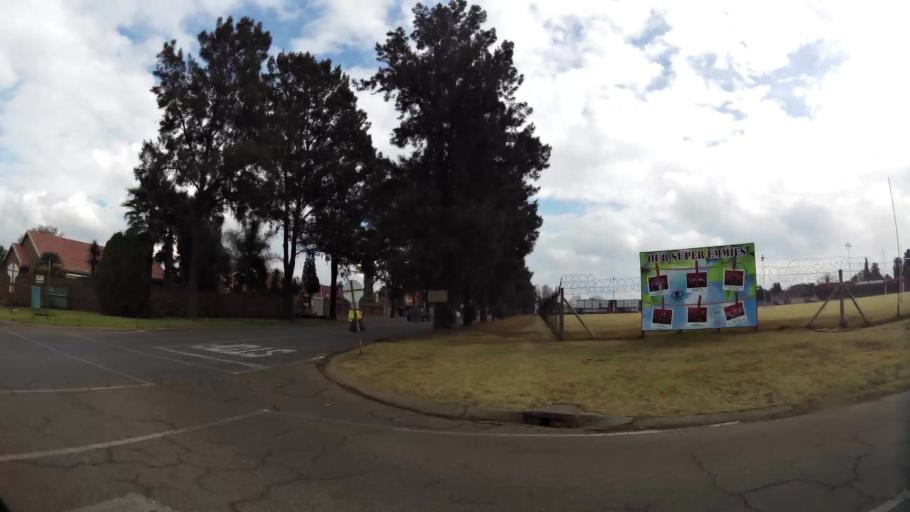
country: ZA
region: Gauteng
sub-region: Sedibeng District Municipality
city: Vanderbijlpark
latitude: -26.7384
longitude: 27.8492
